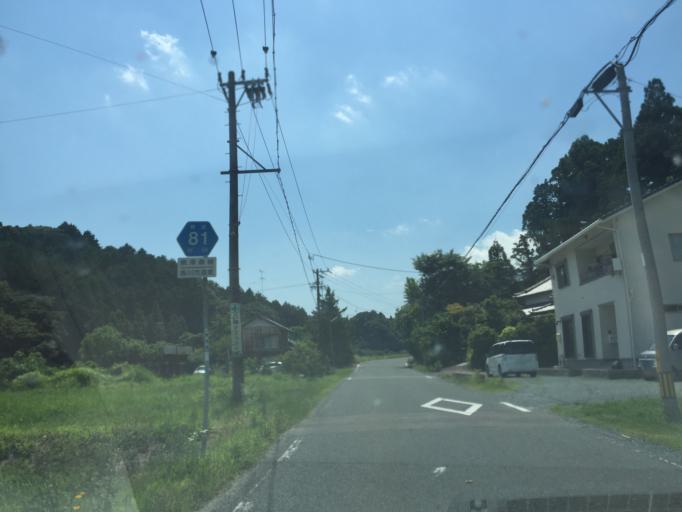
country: JP
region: Shizuoka
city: Mori
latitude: 34.8049
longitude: 137.9742
